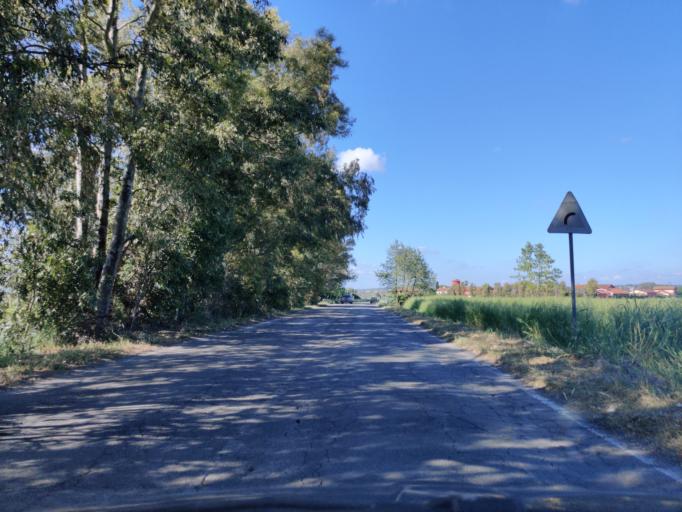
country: IT
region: Latium
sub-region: Citta metropolitana di Roma Capitale
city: Maccarese
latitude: 41.8789
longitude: 12.2139
